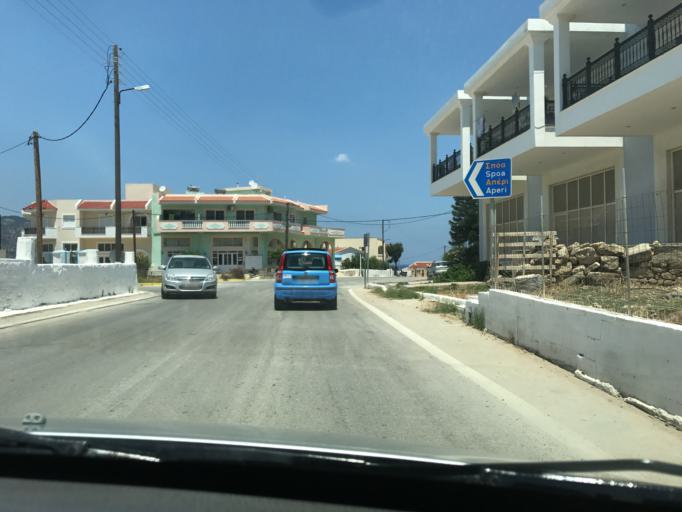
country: GR
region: South Aegean
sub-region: Nomos Dodekanisou
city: Karpathos
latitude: 35.5025
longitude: 27.2107
